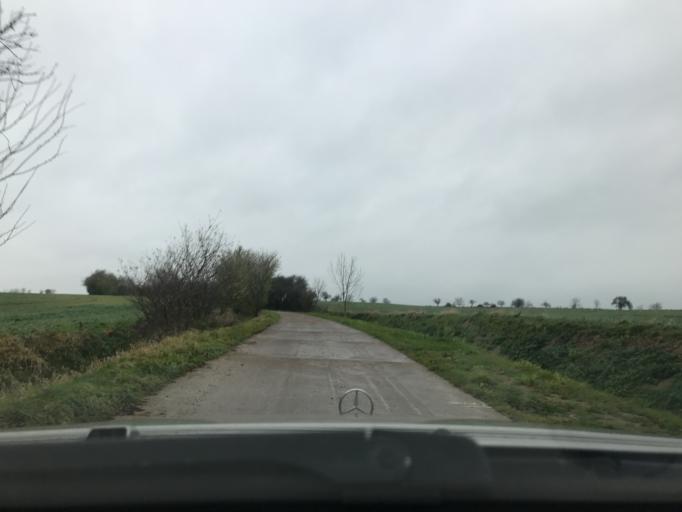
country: DE
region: Thuringia
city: Muehlhausen
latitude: 51.2468
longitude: 10.4037
